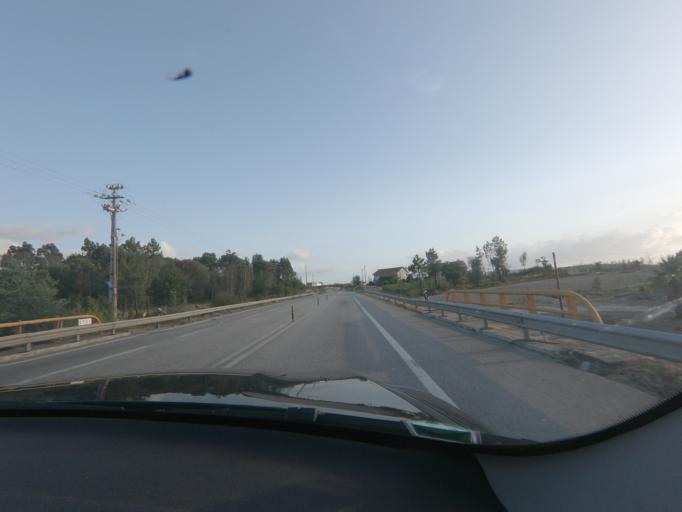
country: PT
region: Viseu
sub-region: Santa Comba Dao
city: Santa Comba Dao
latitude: 40.3649
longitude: -8.1326
